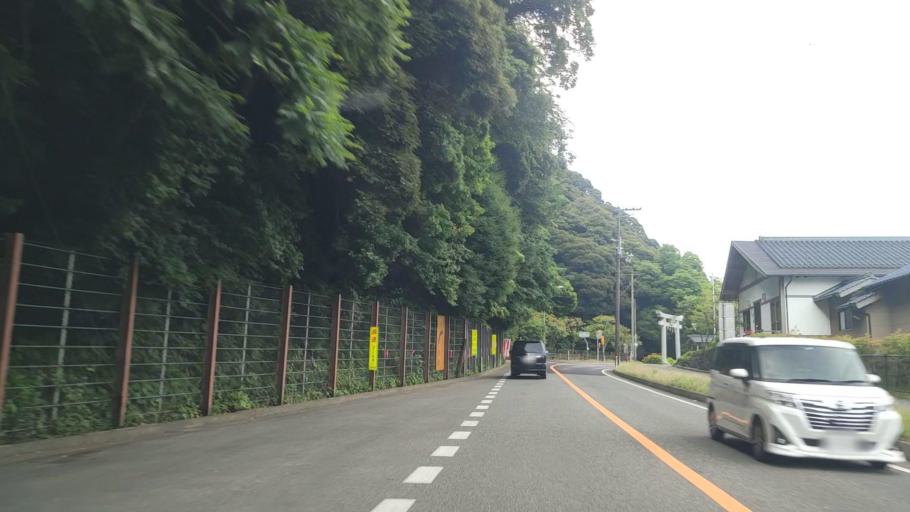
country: JP
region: Hyogo
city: Toyooka
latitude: 35.6413
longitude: 134.8289
